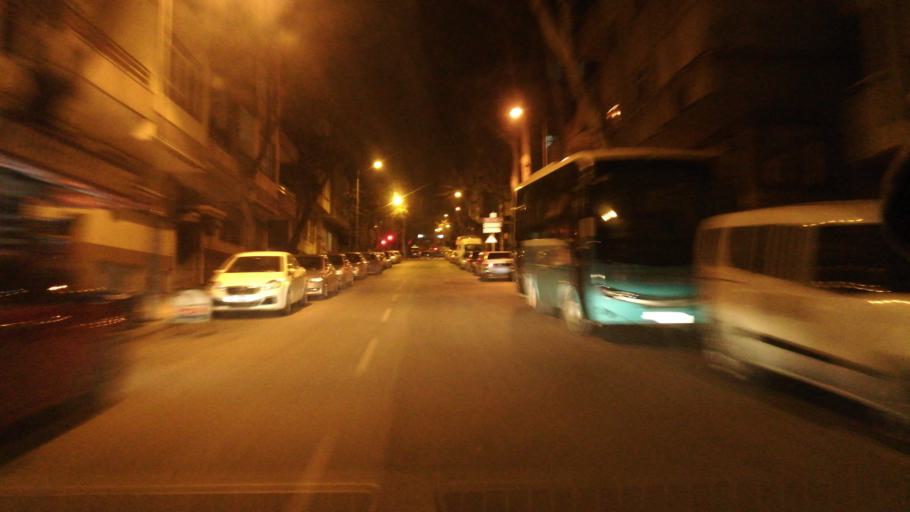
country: TR
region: Kahramanmaras
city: Kahramanmaras
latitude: 37.5915
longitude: 36.9287
